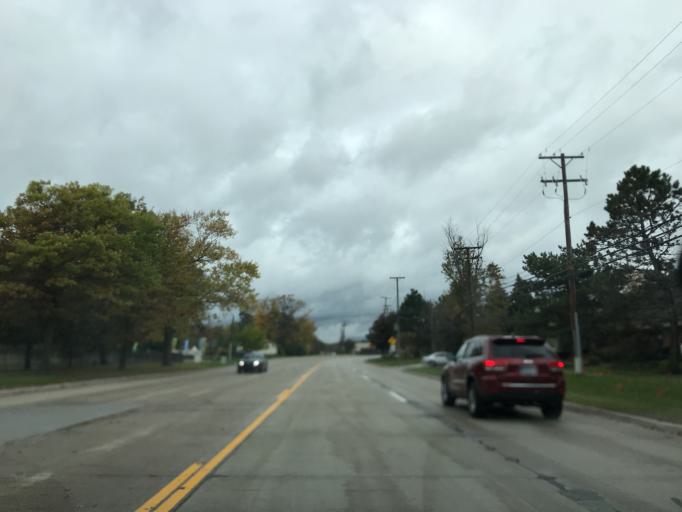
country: US
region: Michigan
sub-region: Oakland County
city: Franklin
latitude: 42.4960
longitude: -83.3028
